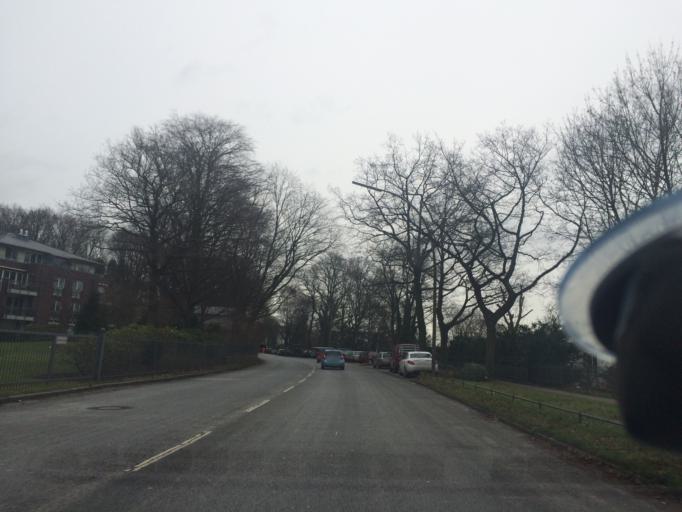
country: DE
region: Hamburg
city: Altona
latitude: 53.5454
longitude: 9.9027
